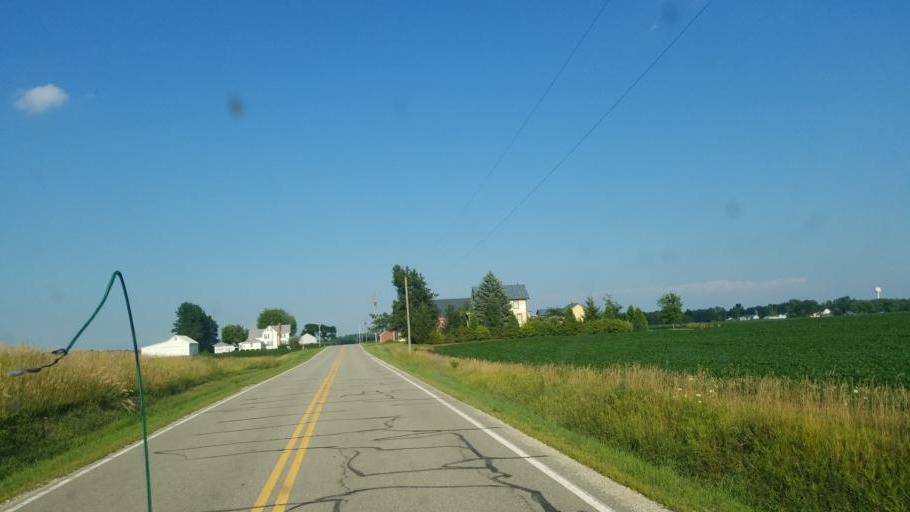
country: US
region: Ohio
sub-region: Crawford County
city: Galion
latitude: 40.7986
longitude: -82.8681
